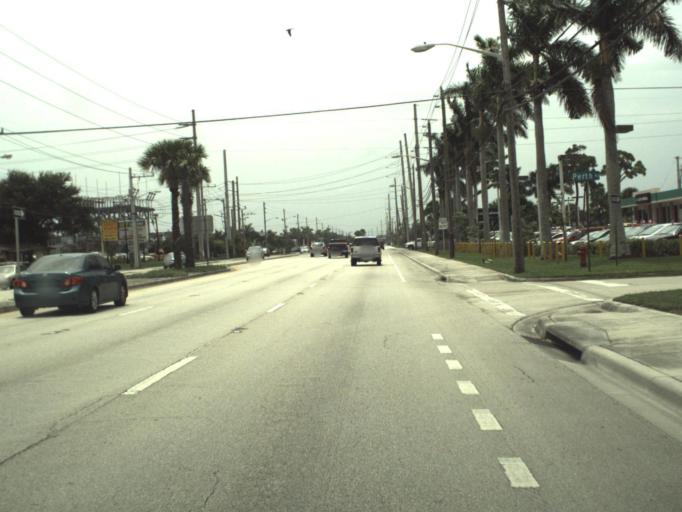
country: US
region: Florida
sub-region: Palm Beach County
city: Royal Palm Estates
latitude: 26.6715
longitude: -80.1125
